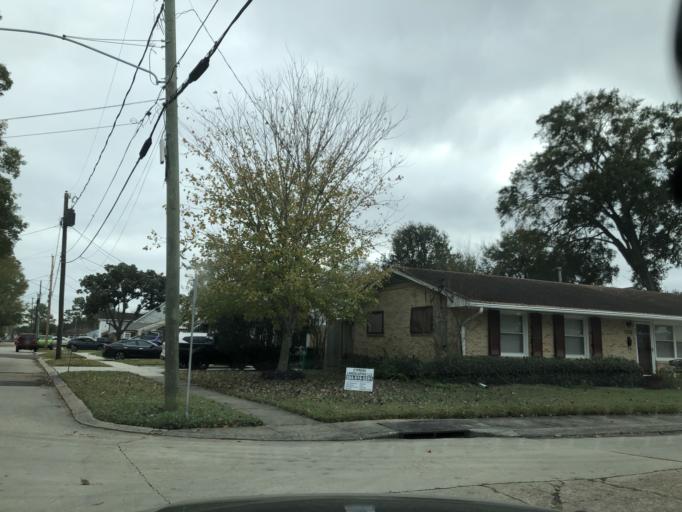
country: US
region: Louisiana
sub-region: Jefferson Parish
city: Metairie Terrace
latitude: 29.9838
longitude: -90.1644
